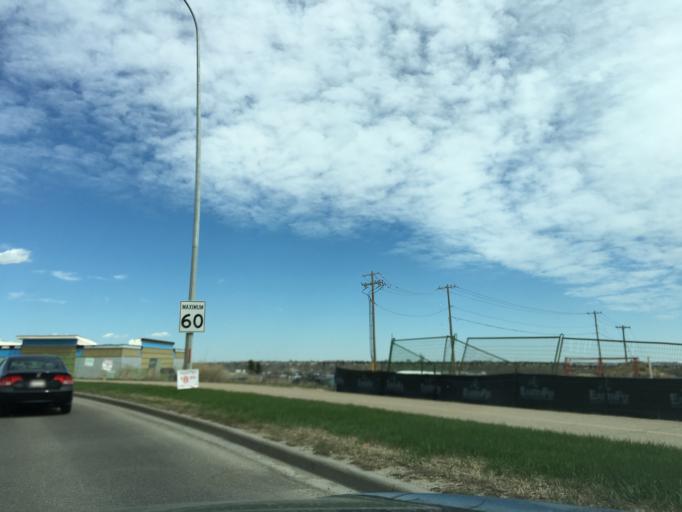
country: CA
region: Alberta
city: Calgary
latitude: 50.9812
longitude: -114.0486
